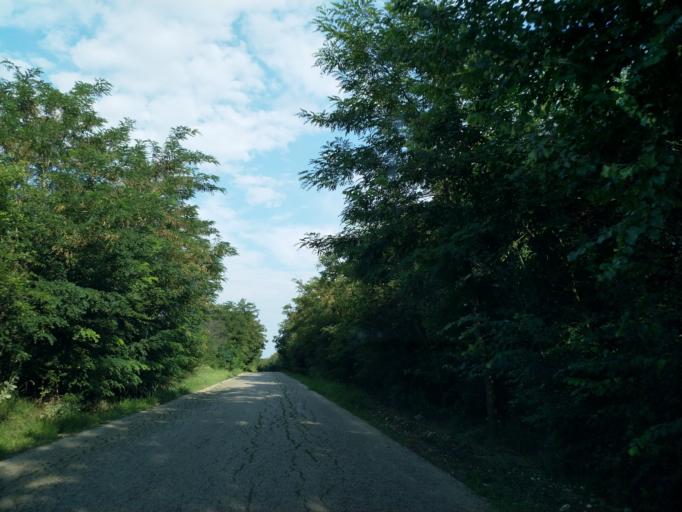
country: RS
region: Central Serbia
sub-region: Pomoravski Okrug
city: Jagodina
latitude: 43.9932
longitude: 21.1996
